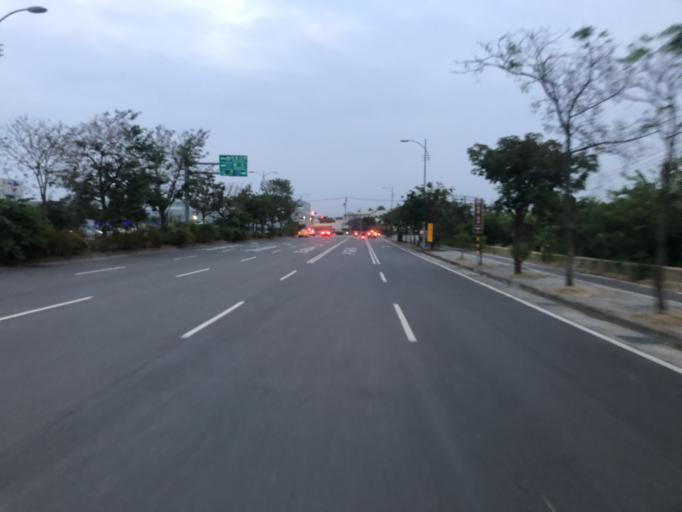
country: TW
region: Taiwan
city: Yujing
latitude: 23.1117
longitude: 120.3166
